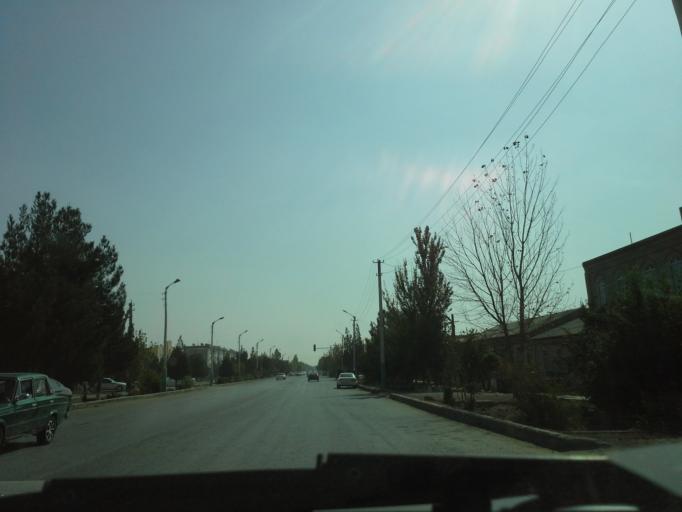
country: TM
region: Lebap
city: Atamyrat
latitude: 37.8432
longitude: 65.1997
